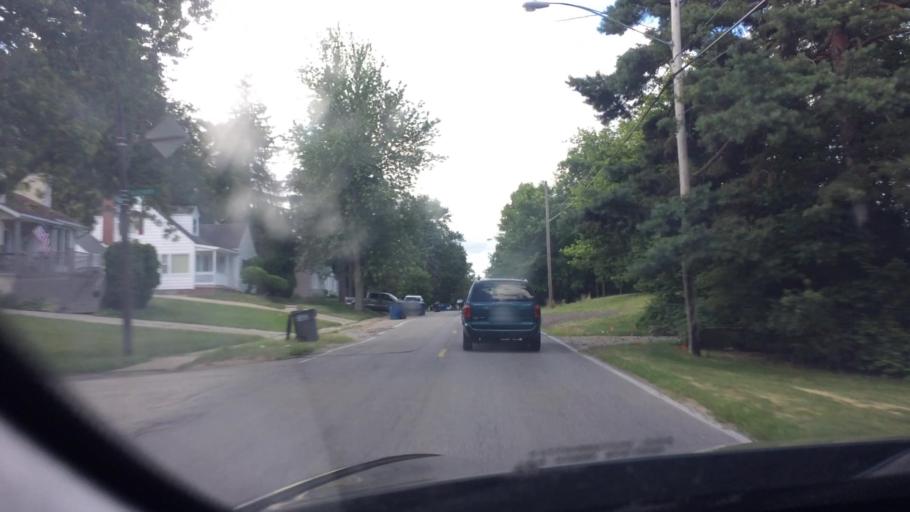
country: US
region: Ohio
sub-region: Lucas County
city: Ottawa Hills
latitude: 41.6480
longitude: -83.6407
